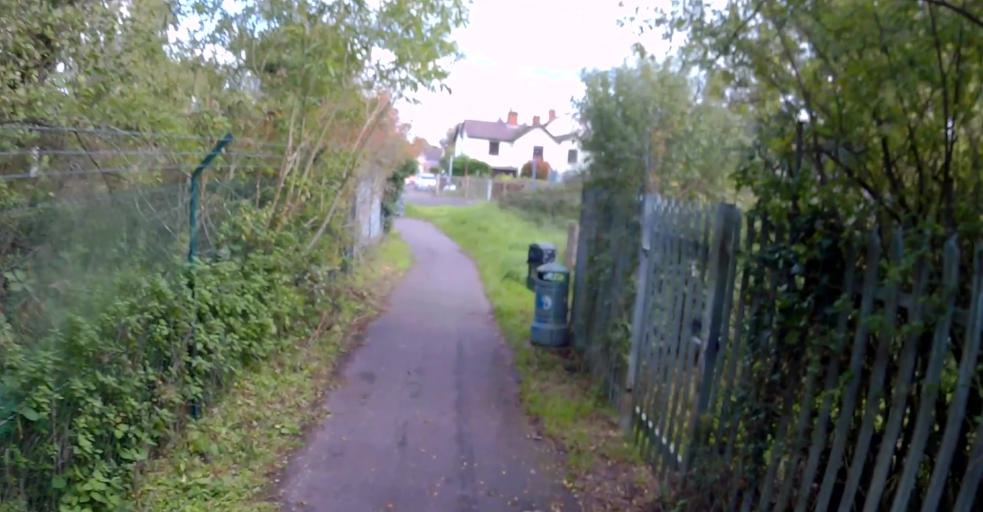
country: GB
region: England
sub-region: Surrey
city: Frimley
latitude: 51.3030
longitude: -0.7341
